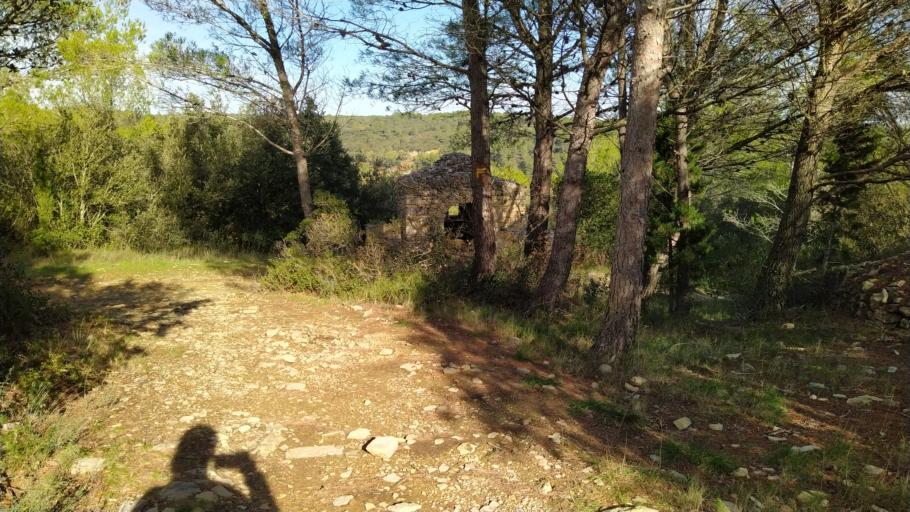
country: FR
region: Languedoc-Roussillon
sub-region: Departement du Gard
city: Poulx
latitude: 43.8723
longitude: 4.4031
